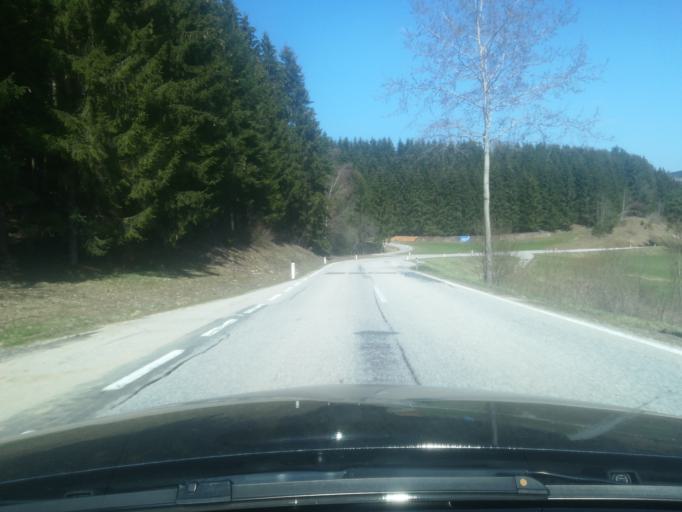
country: AT
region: Upper Austria
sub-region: Politischer Bezirk Perg
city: Sankt Georgen am Walde
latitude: 48.4236
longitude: 14.7718
